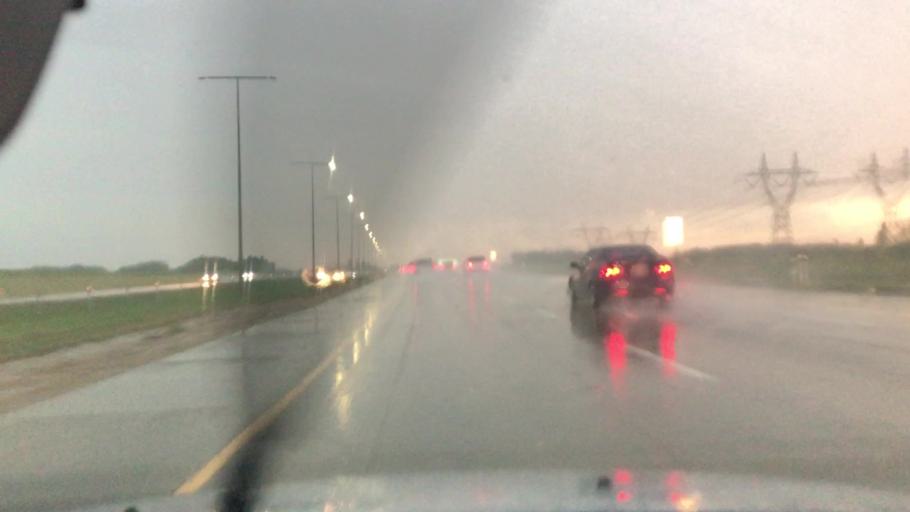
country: CA
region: Alberta
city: Edmonton
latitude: 53.4331
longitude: -113.5447
